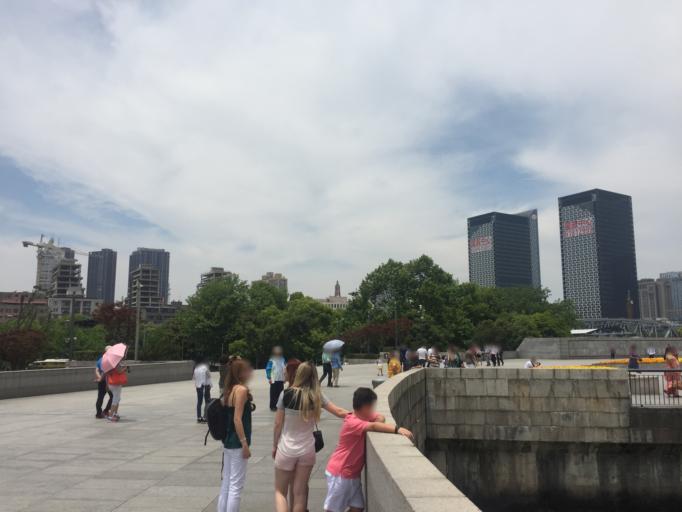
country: CN
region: Shanghai Shi
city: Hongkou
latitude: 31.2439
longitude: 121.4869
